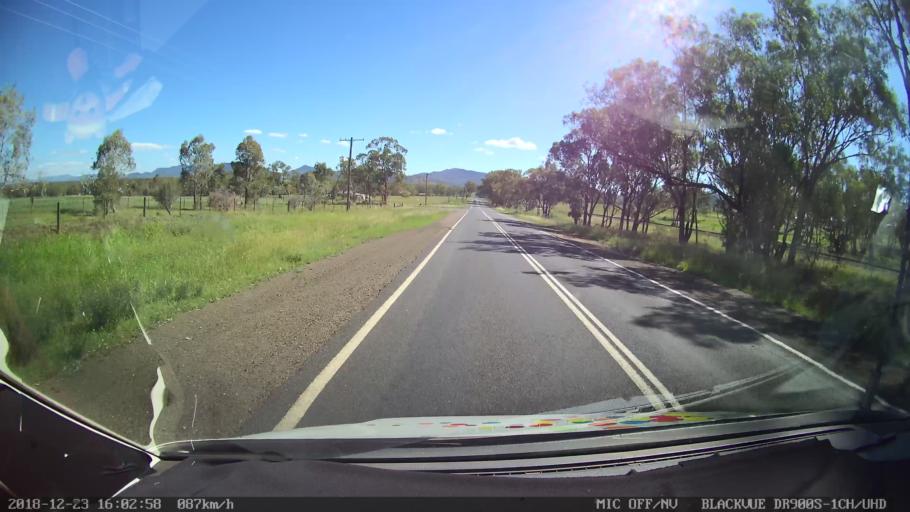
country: AU
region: New South Wales
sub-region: Tamworth Municipality
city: Phillip
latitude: -31.2380
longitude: 150.8047
